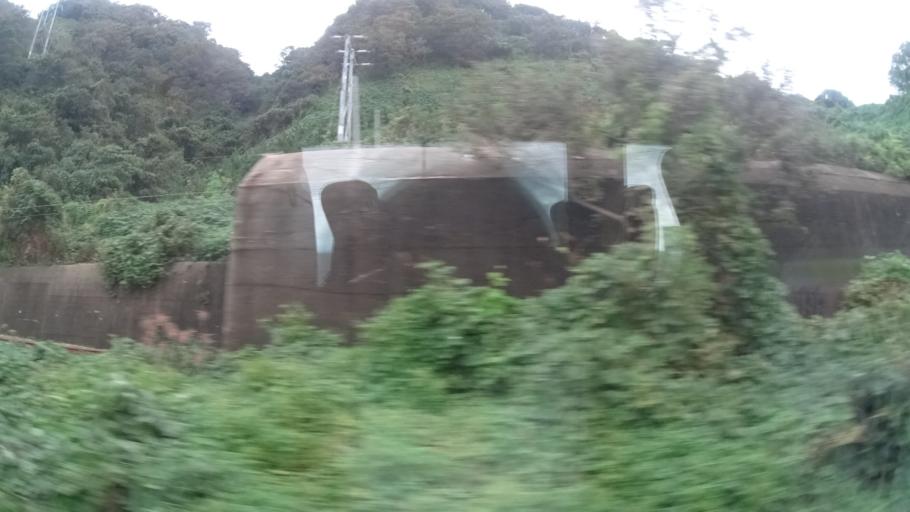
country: JP
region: Yamagata
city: Tsuruoka
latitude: 38.5809
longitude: 139.5602
